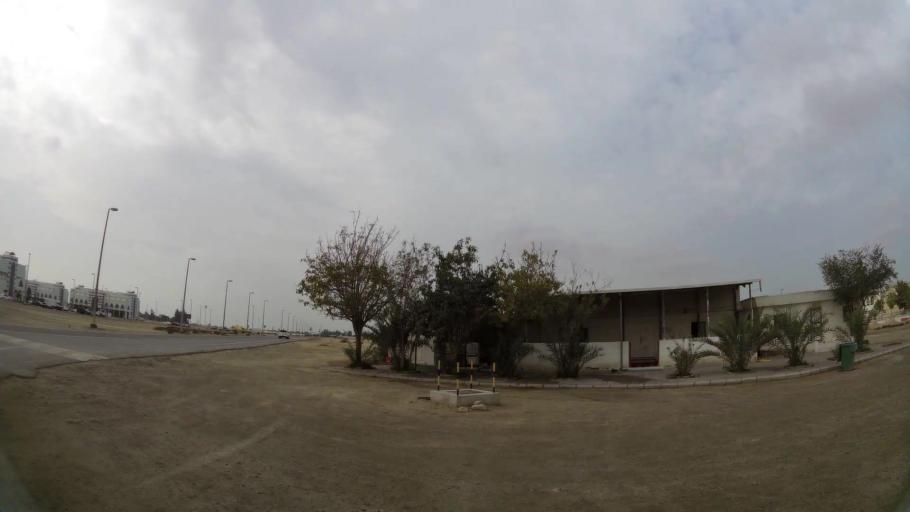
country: AE
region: Abu Dhabi
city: Abu Dhabi
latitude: 24.6280
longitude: 54.7134
